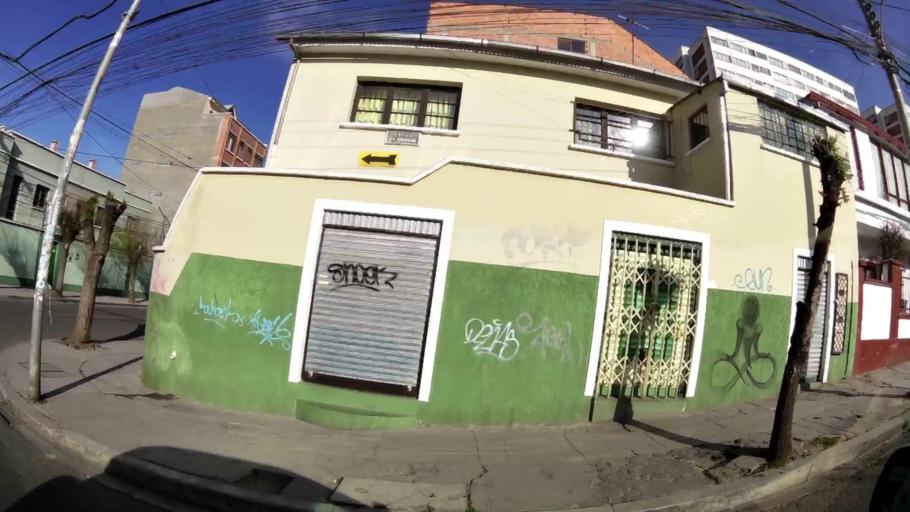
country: BO
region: La Paz
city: La Paz
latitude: -16.5036
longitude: -68.1181
